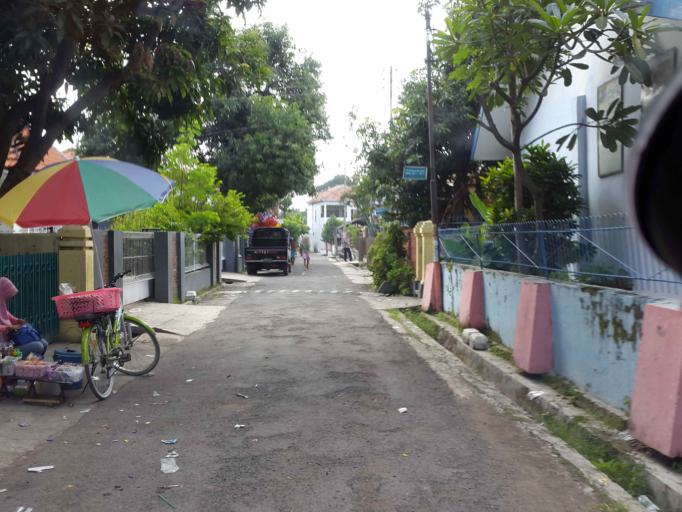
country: ID
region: Central Java
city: Pemalang
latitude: -6.9015
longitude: 109.3841
